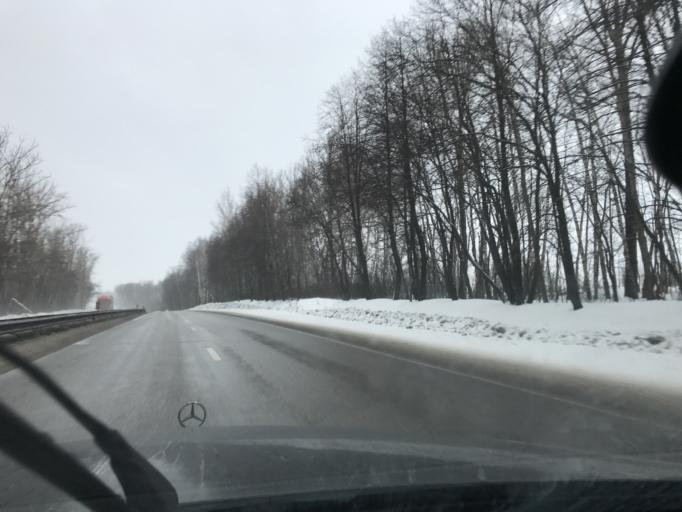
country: RU
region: Vladimir
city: Novovyazniki
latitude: 56.1897
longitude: 42.3901
